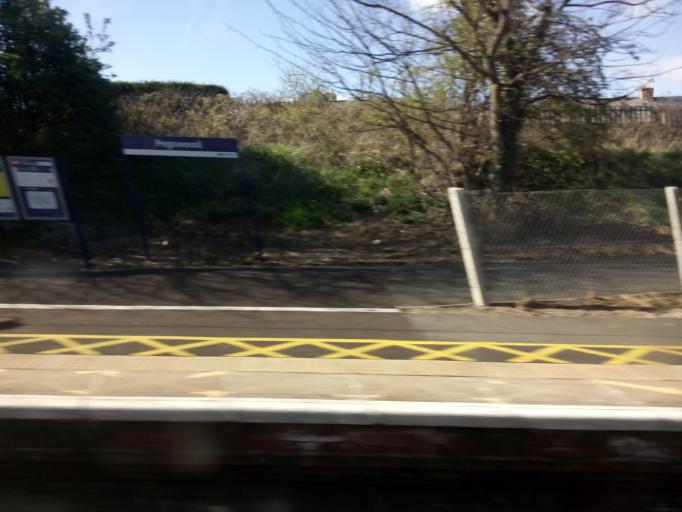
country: GB
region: England
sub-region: Northumberland
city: Pegswood
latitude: 55.1783
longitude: -1.6437
